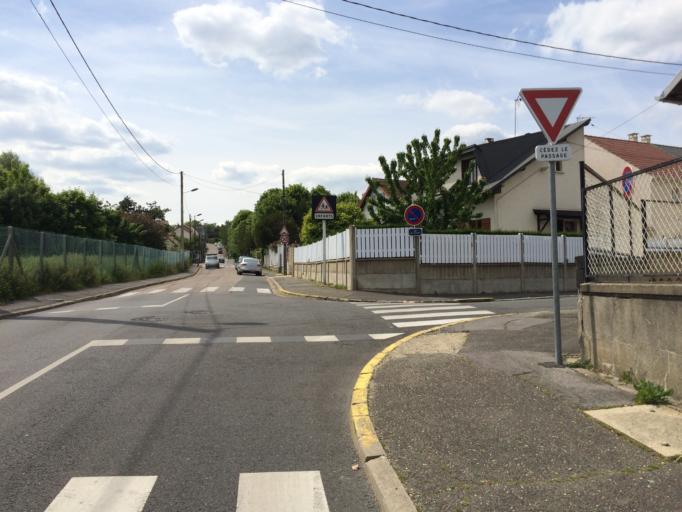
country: FR
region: Ile-de-France
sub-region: Departement de l'Essonne
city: Palaiseau
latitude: 48.7249
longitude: 2.2397
